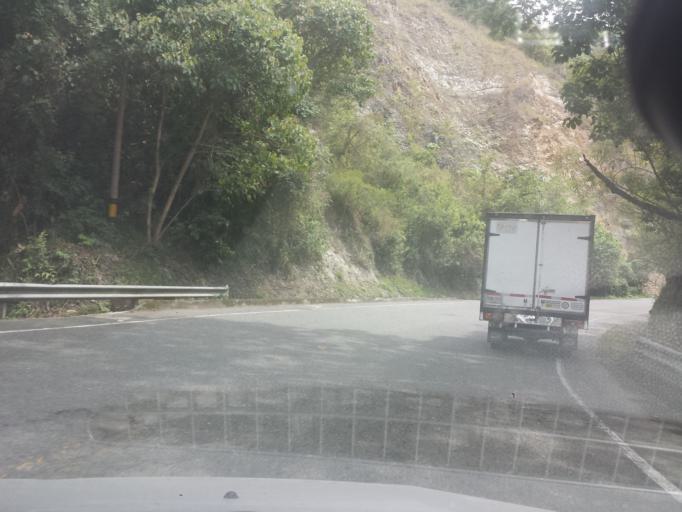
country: CO
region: Antioquia
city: Liborina
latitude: 6.6296
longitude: -75.8736
